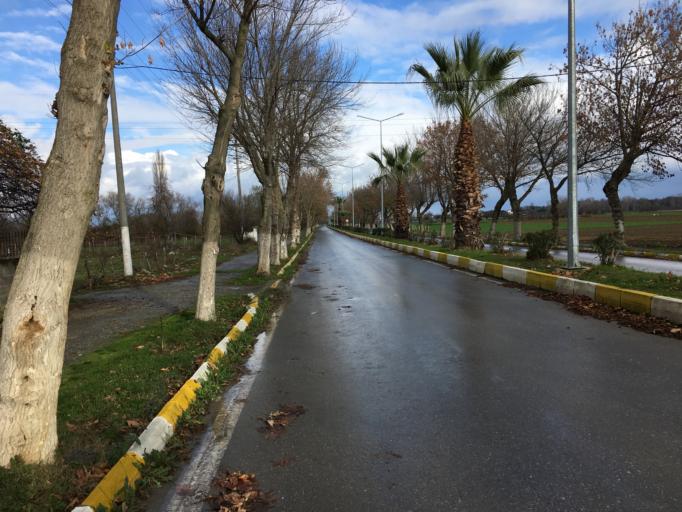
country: TR
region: Samsun
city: Alacam
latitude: 41.6226
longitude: 35.6081
